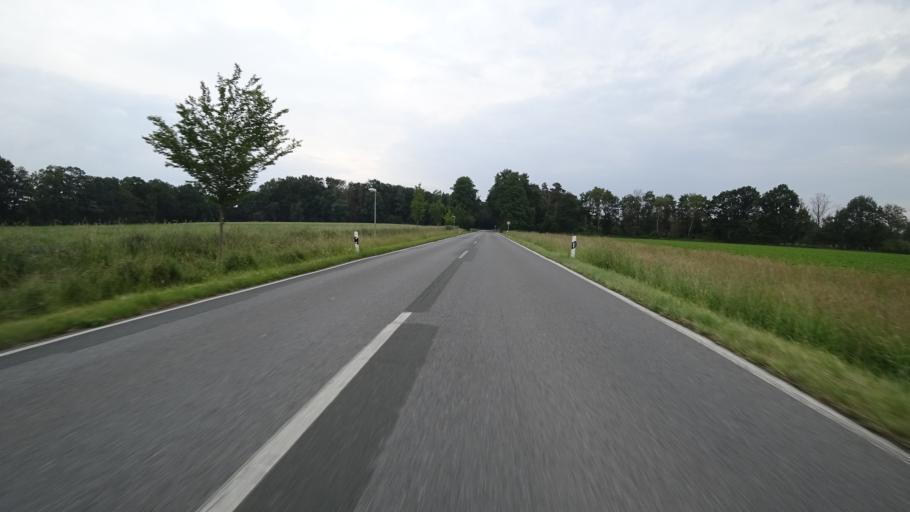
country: DE
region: North Rhine-Westphalia
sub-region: Regierungsbezirk Detmold
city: Guetersloh
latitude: 51.9373
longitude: 8.3798
